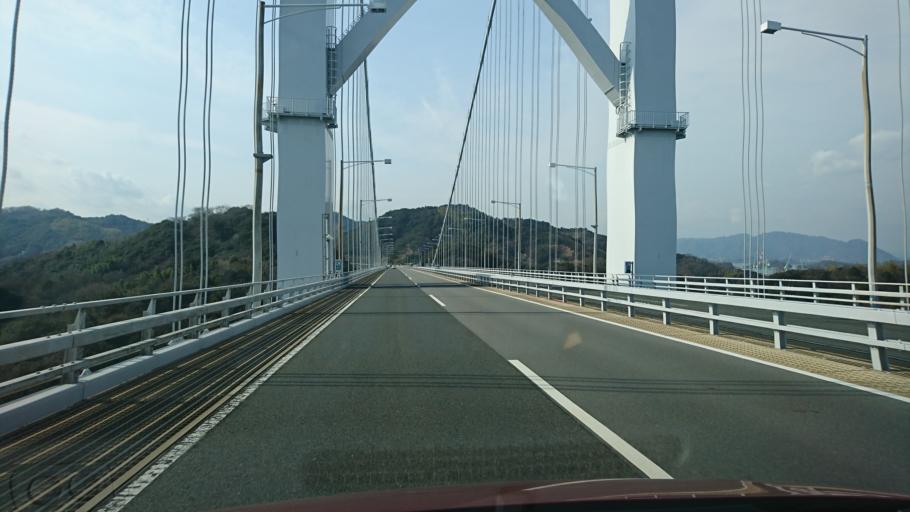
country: JP
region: Hiroshima
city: Onomichi
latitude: 34.3557
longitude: 133.1770
